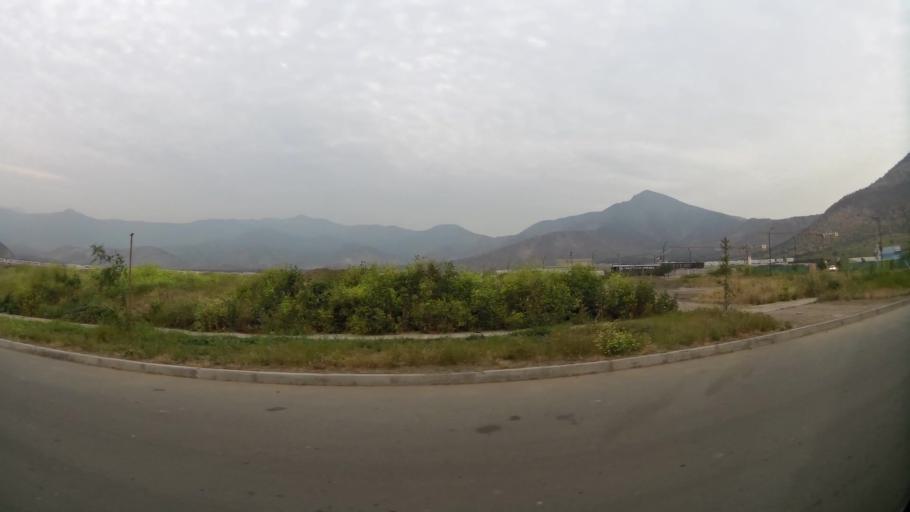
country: CL
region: Santiago Metropolitan
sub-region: Provincia de Chacabuco
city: Chicureo Abajo
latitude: -33.3174
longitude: -70.6535
